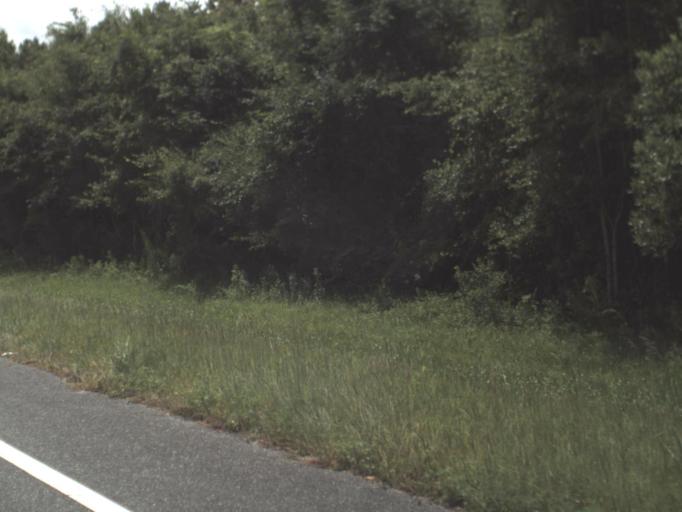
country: US
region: Florida
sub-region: Columbia County
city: Watertown
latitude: 30.1439
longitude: -82.5429
